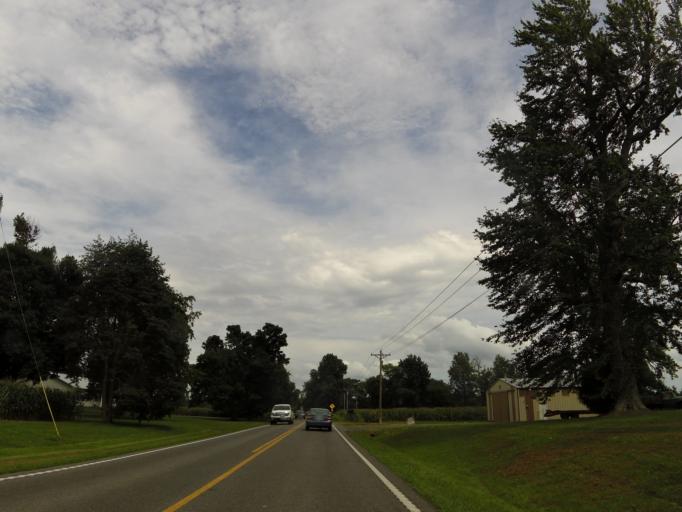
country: US
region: Kentucky
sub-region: McCracken County
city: Massac
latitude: 37.0053
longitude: -88.8410
